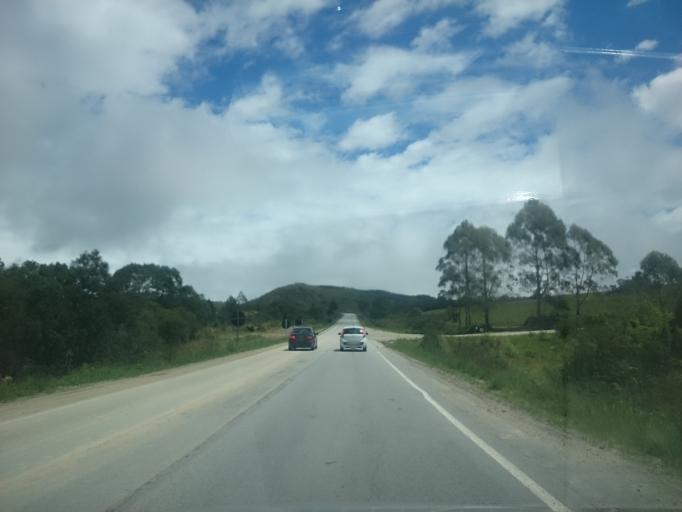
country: BR
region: Santa Catarina
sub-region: Anitapolis
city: Anitapolis
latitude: -27.6827
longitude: -49.1149
